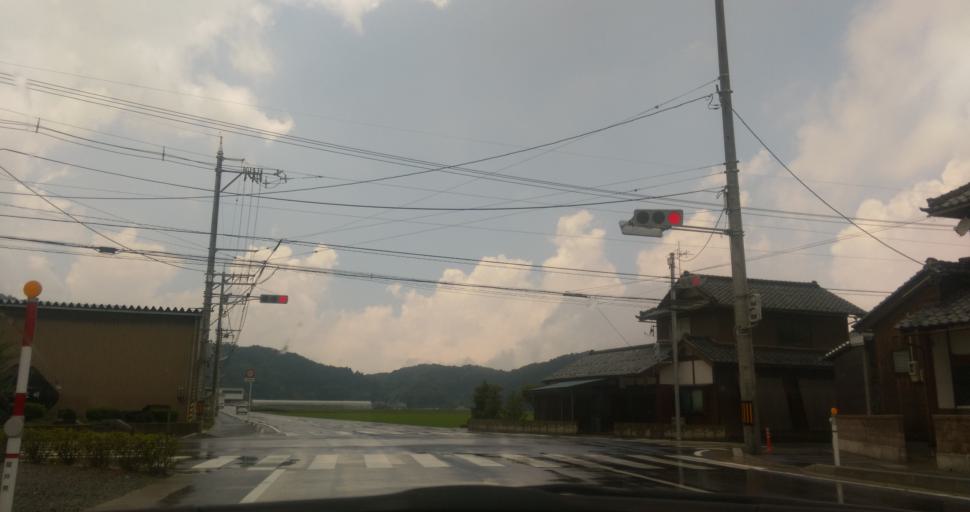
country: JP
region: Fukui
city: Fukui-shi
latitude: 36.0152
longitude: 136.2019
